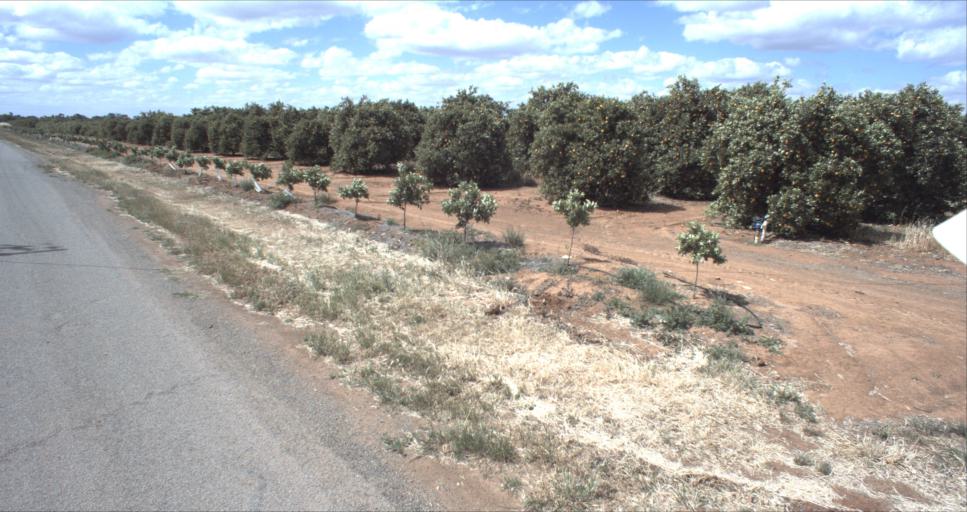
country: AU
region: New South Wales
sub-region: Leeton
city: Leeton
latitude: -34.5844
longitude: 146.3916
